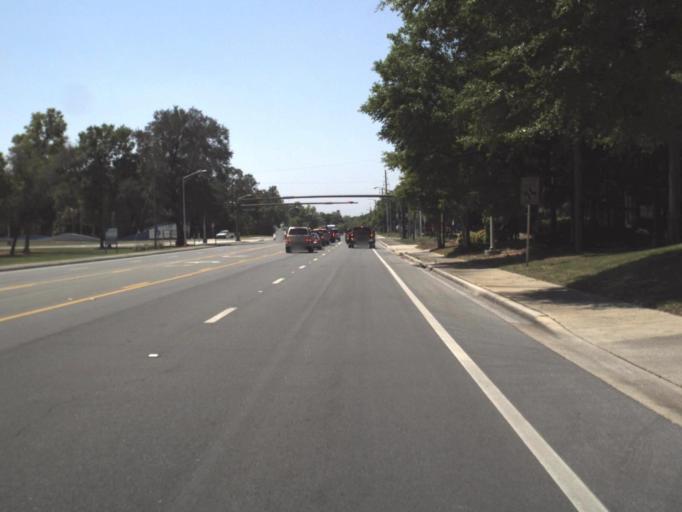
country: US
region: Florida
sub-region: Escambia County
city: Ferry Pass
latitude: 30.4762
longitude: -87.1985
